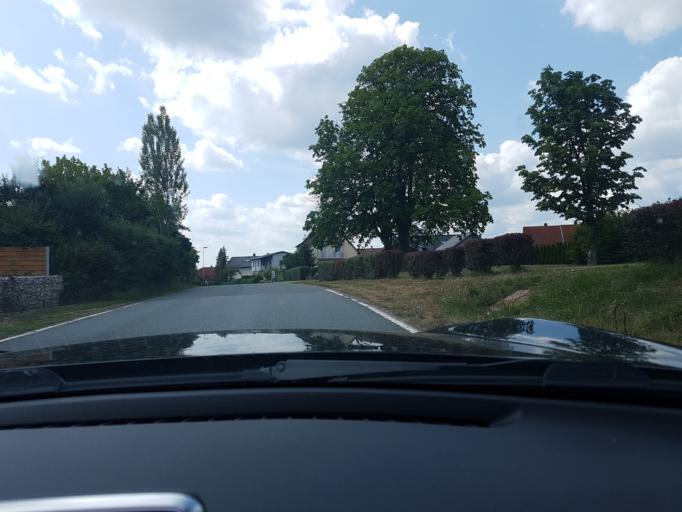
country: DE
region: Baden-Wuerttemberg
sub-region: Karlsruhe Region
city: Limbach
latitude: 49.4263
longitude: 9.2091
